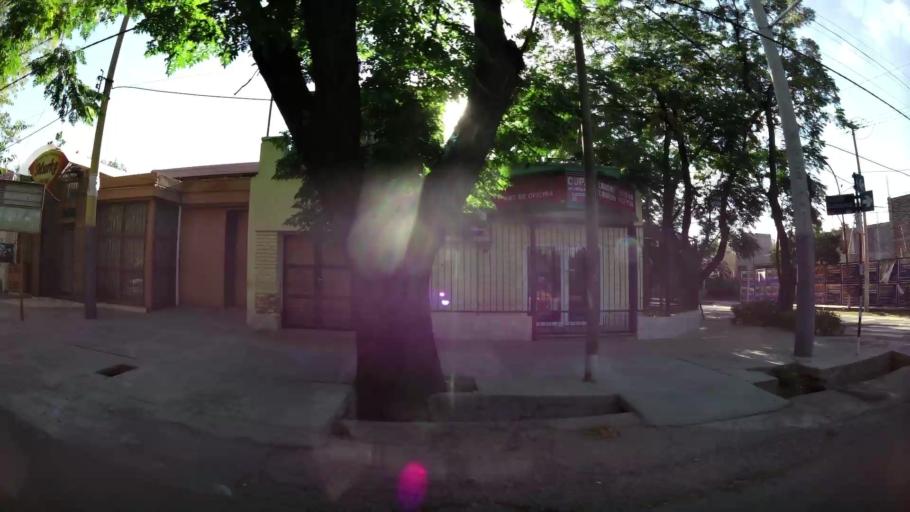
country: AR
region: Mendoza
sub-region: Departamento de Godoy Cruz
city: Godoy Cruz
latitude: -32.9125
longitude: -68.8299
